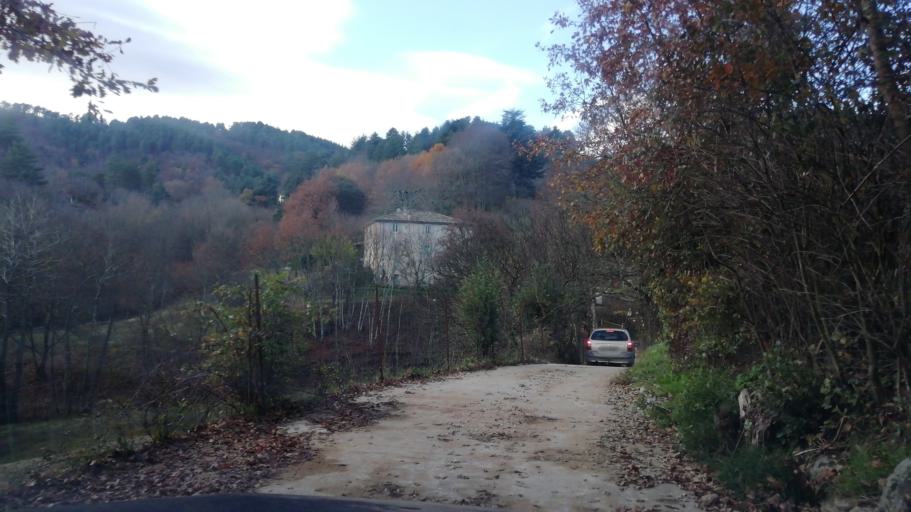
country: FR
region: Languedoc-Roussillon
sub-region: Departement du Gard
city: Lasalle
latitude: 44.0306
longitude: 3.8560
